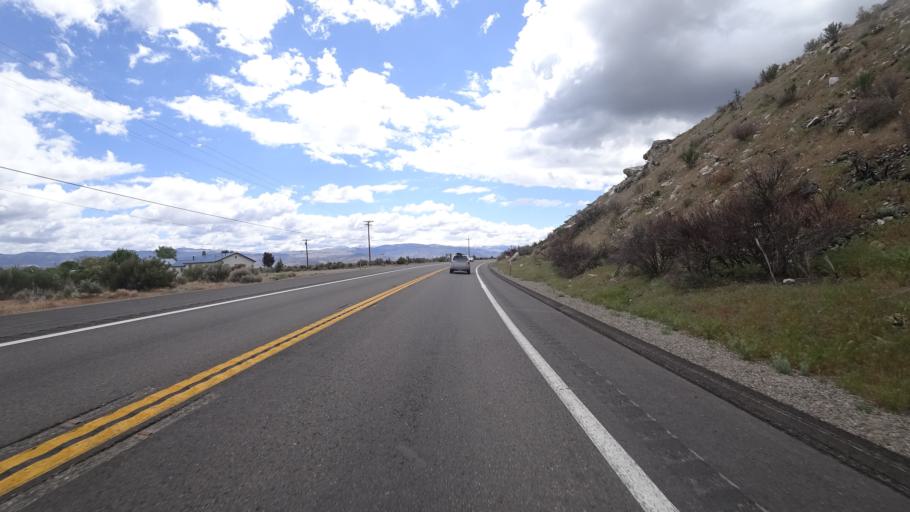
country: US
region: Nevada
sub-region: Lyon County
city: Smith Valley
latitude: 38.6478
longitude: -119.5304
